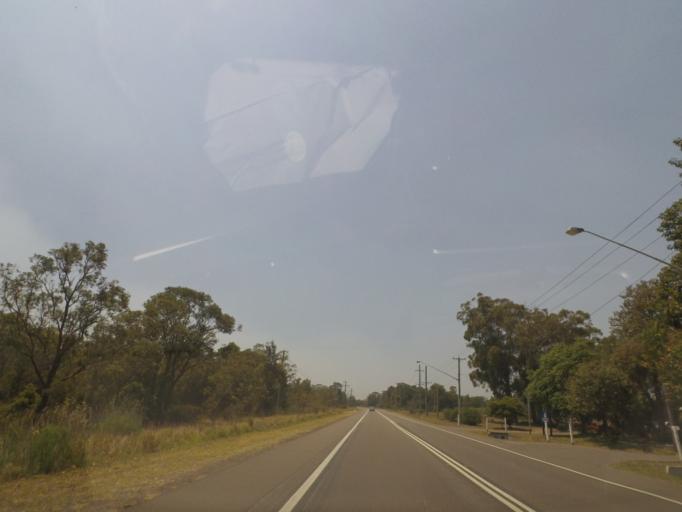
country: AU
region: New South Wales
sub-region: Newcastle
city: Mayfield West
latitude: -32.8309
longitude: 151.7174
